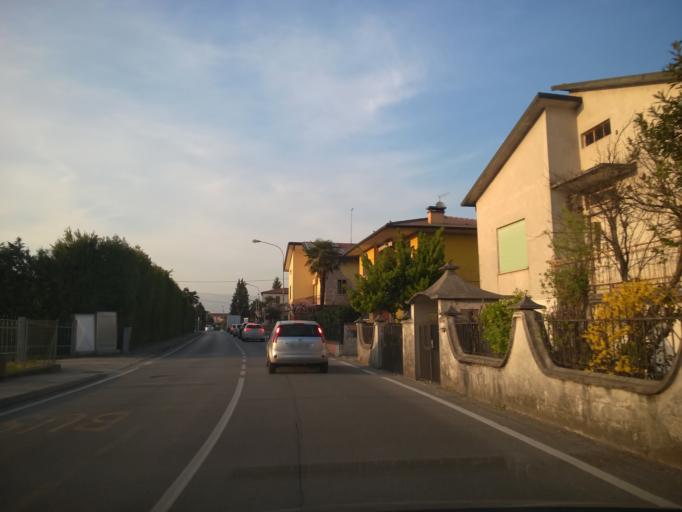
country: IT
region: Veneto
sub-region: Provincia di Vicenza
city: Caldogno-Rettorgole-Cresole
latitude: 45.5988
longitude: 11.5278
